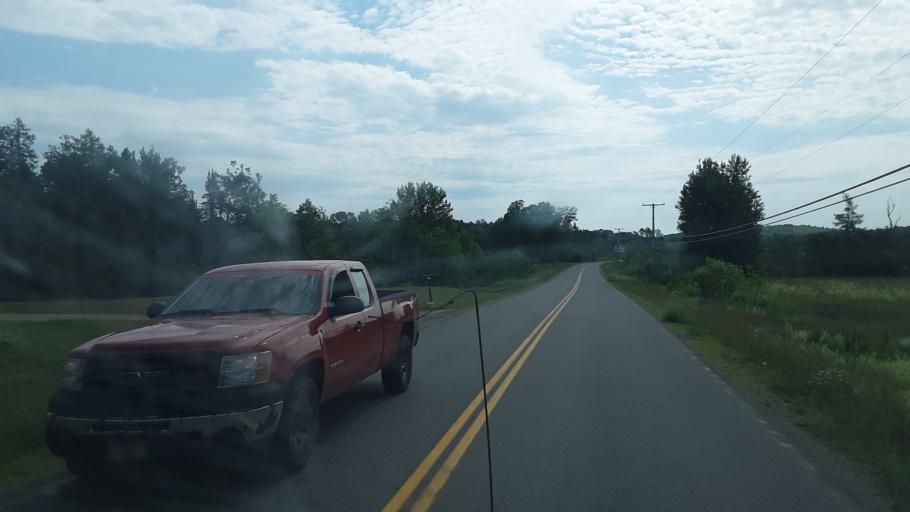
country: US
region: Maine
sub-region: Waldo County
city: Frankfort
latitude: 44.6145
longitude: -68.9326
